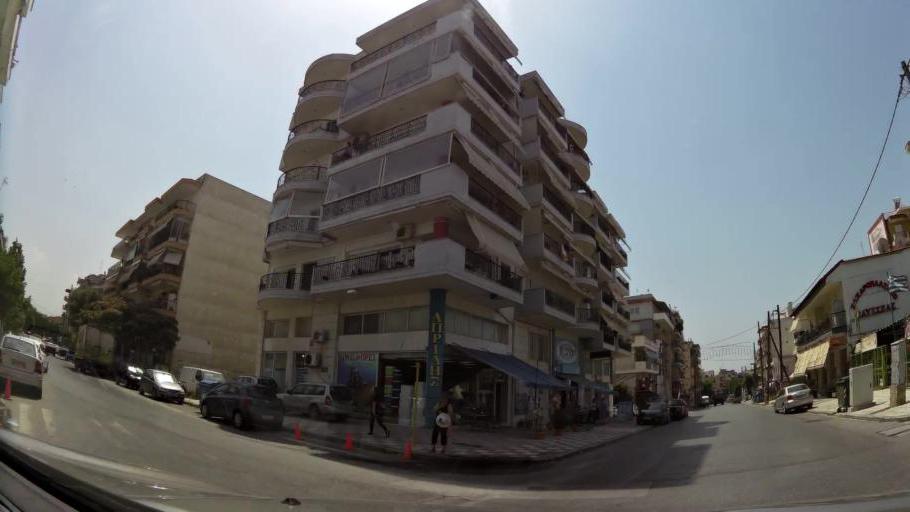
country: GR
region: Central Macedonia
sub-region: Nomos Thessalonikis
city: Evosmos
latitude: 40.6762
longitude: 22.9062
